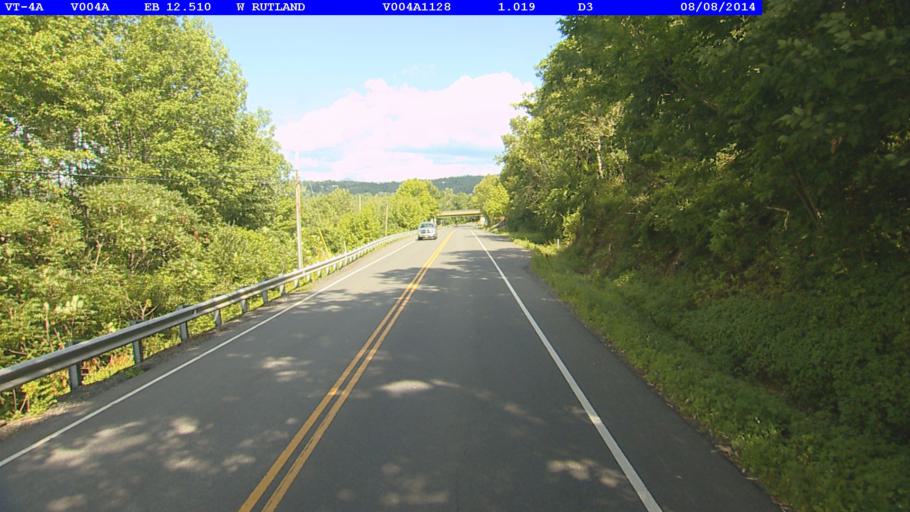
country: US
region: Vermont
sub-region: Rutland County
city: West Rutland
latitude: 43.6043
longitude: -73.0686
